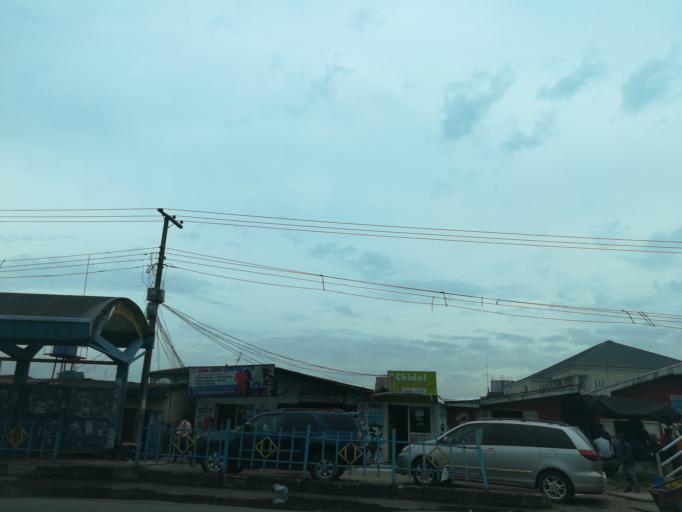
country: NG
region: Rivers
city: Port Harcourt
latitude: 4.8123
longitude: 7.0100
